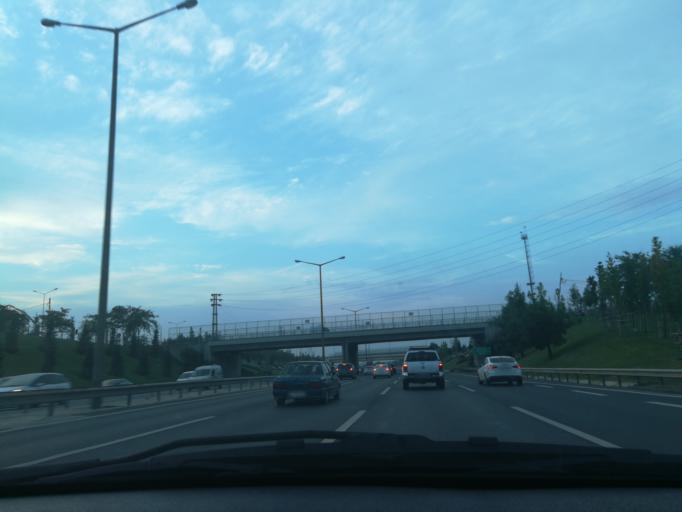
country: TR
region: Istanbul
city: Umraniye
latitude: 41.0517
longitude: 29.1212
